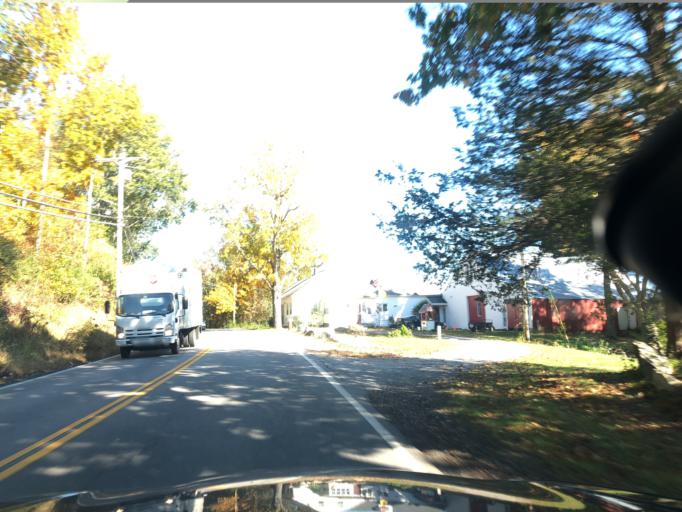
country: US
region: New Hampshire
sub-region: Rockingham County
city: Exeter
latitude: 43.0092
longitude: -70.9453
